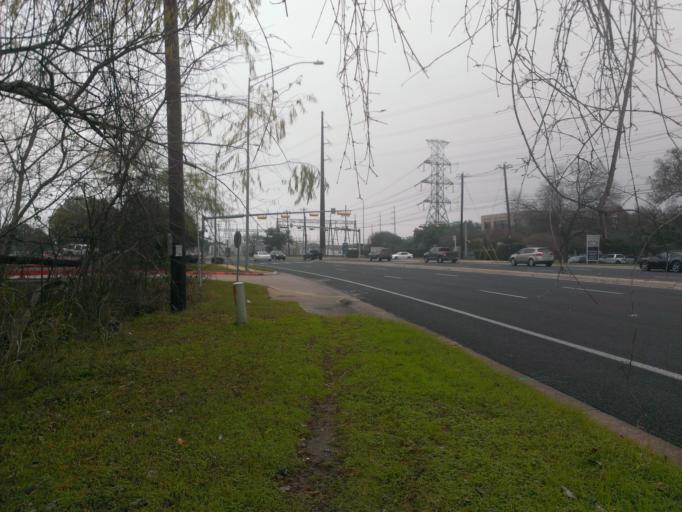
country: US
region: Texas
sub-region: Williamson County
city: Jollyville
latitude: 30.3999
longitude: -97.7416
